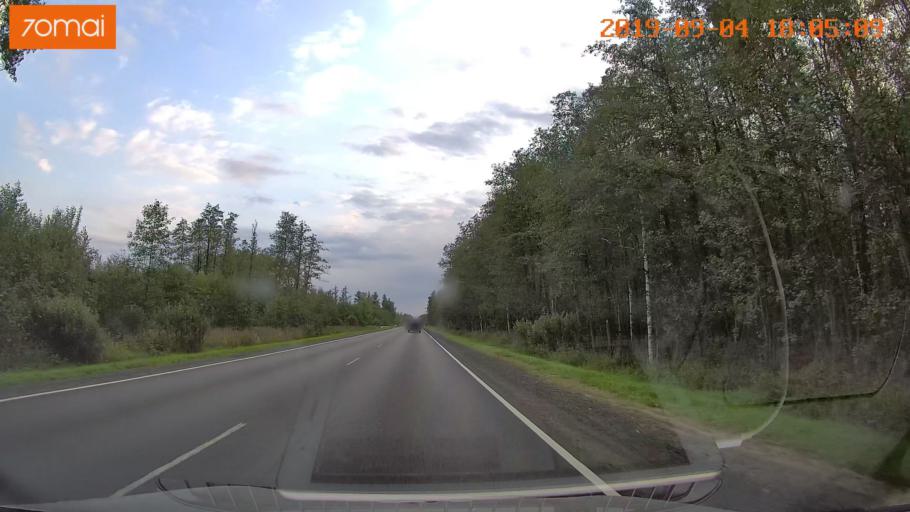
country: RU
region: Moskovskaya
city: Il'inskiy Pogost
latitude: 55.4444
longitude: 38.8301
